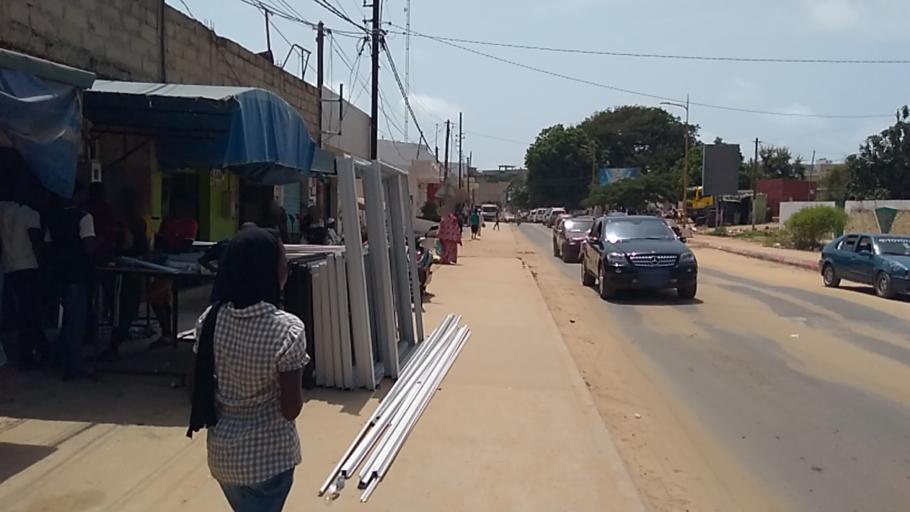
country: SN
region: Dakar
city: Mermoz Boabab
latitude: 14.7205
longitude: -17.4909
